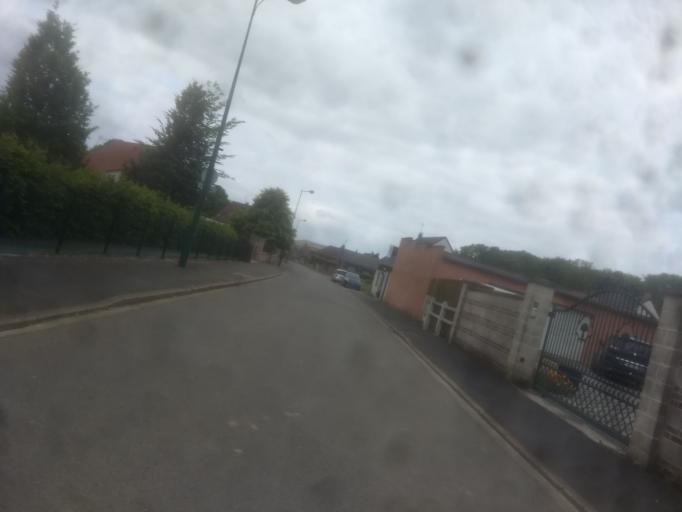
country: FR
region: Nord-Pas-de-Calais
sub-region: Departement du Pas-de-Calais
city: Tilloy-les-Mofflaines
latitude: 50.2721
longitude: 2.8169
